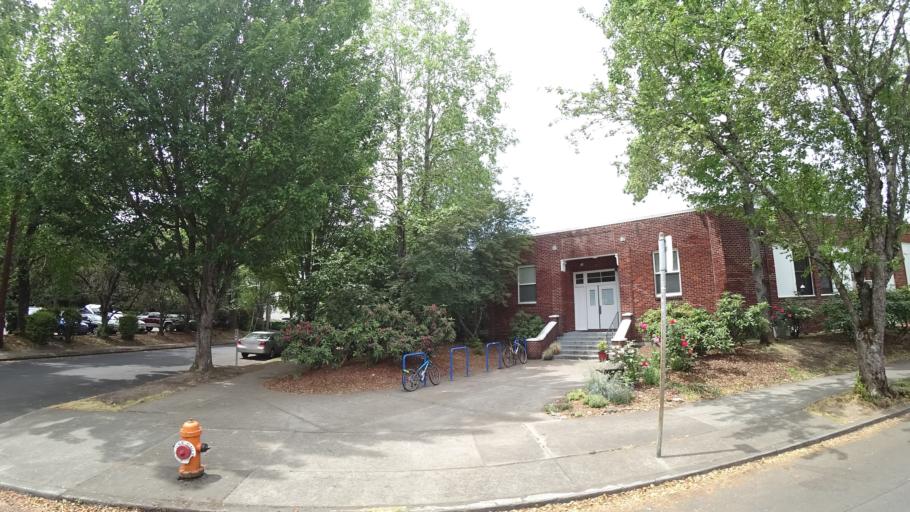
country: US
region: Oregon
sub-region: Multnomah County
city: Lents
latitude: 45.5239
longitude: -122.6121
